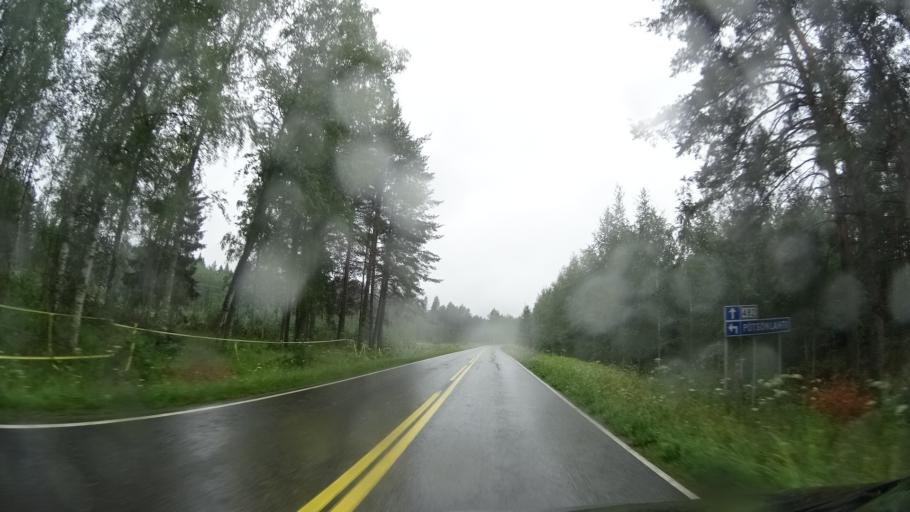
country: FI
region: North Karelia
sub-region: Keski-Karjala
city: Raeaekkylae
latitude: 62.3056
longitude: 29.5495
